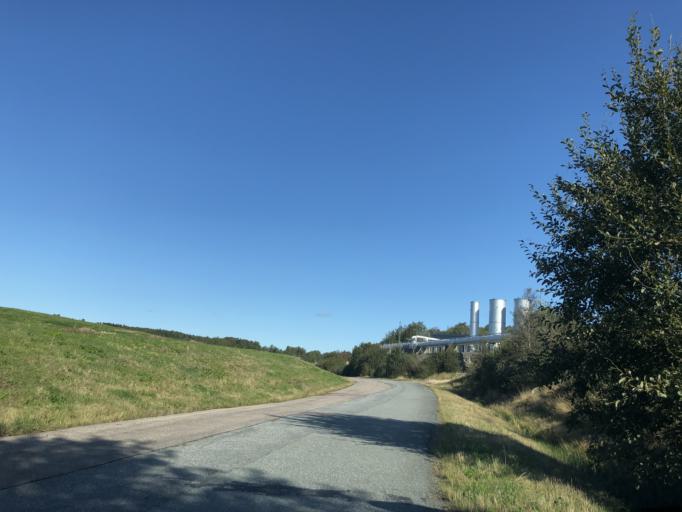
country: SE
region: Vaestra Goetaland
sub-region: Goteborg
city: Torslanda
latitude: 57.7131
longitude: 11.8054
